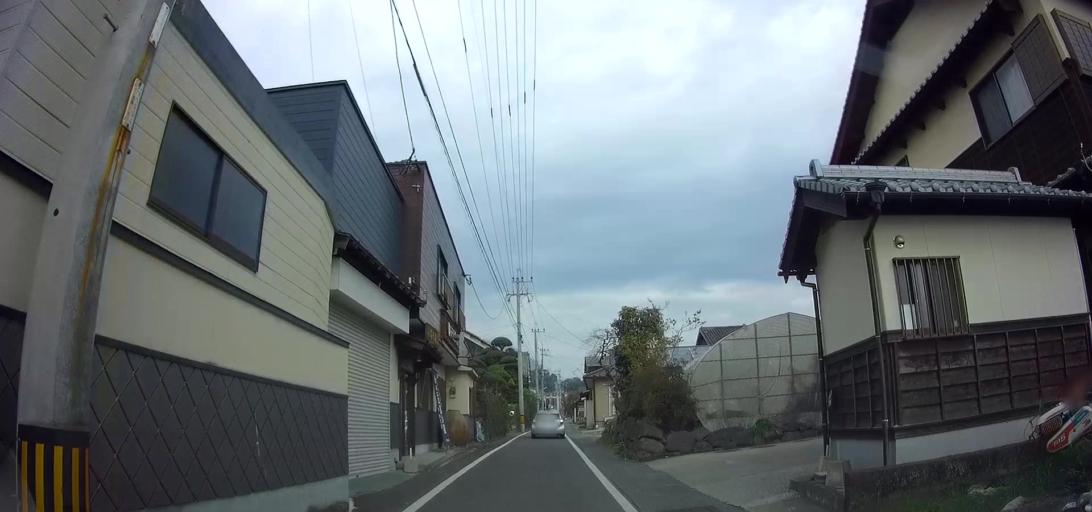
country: JP
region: Nagasaki
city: Shimabara
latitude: 32.6700
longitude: 130.3014
